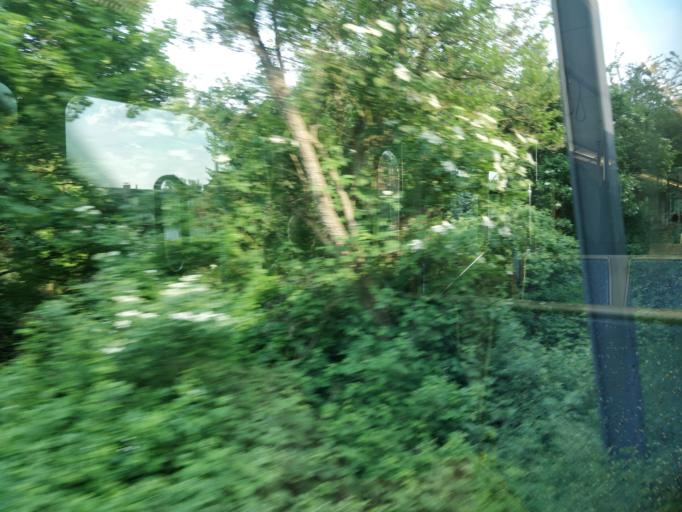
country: DE
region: North Rhine-Westphalia
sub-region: Regierungsbezirk Koln
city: Bilderstoeckchen
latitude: 50.9713
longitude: 6.9050
